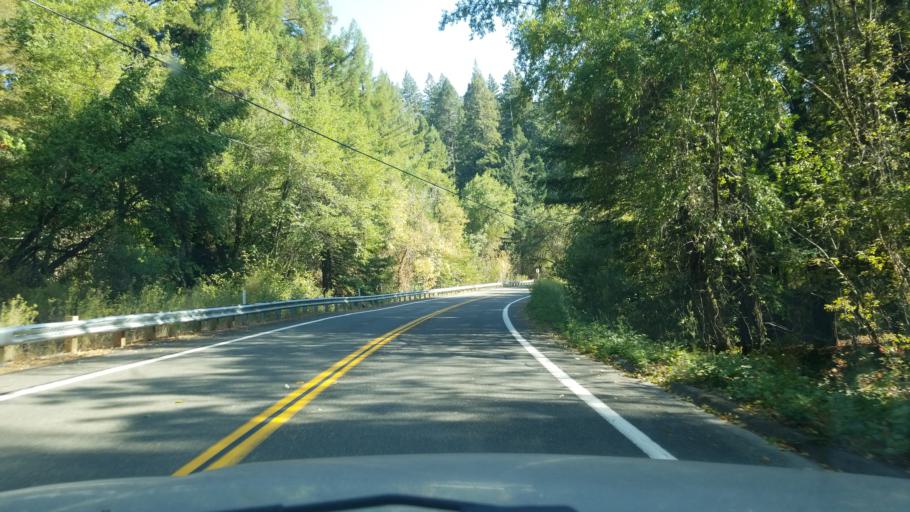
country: US
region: California
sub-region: Humboldt County
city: Redway
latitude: 40.2207
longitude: -123.7865
